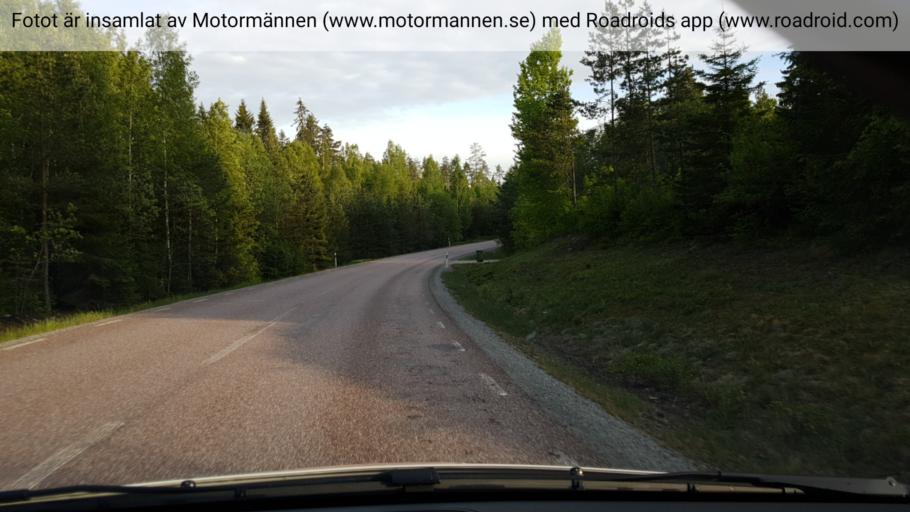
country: SE
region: Vaestmanland
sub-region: Skinnskattebergs Kommun
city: Skinnskatteberg
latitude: 59.8380
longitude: 15.8420
